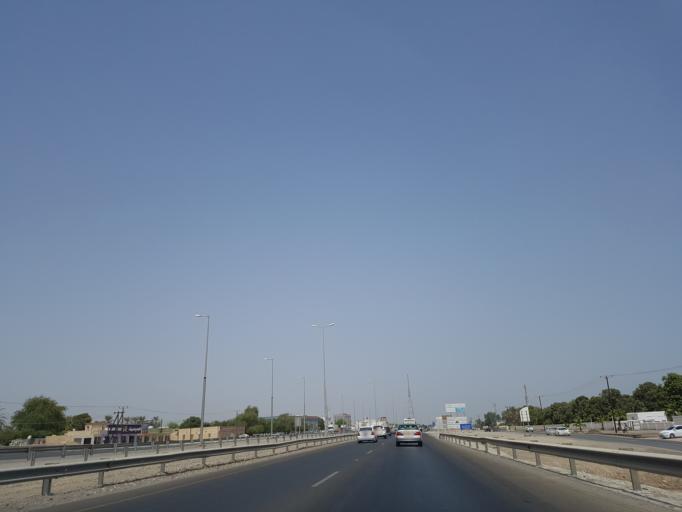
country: OM
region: Al Batinah
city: Saham
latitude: 24.1369
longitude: 56.8827
